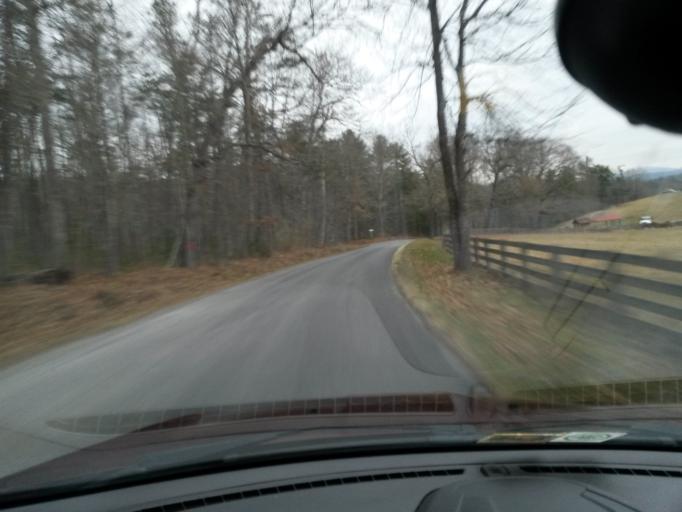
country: US
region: Virginia
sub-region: Bath County
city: Warm Springs
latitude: 38.0324
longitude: -79.7033
